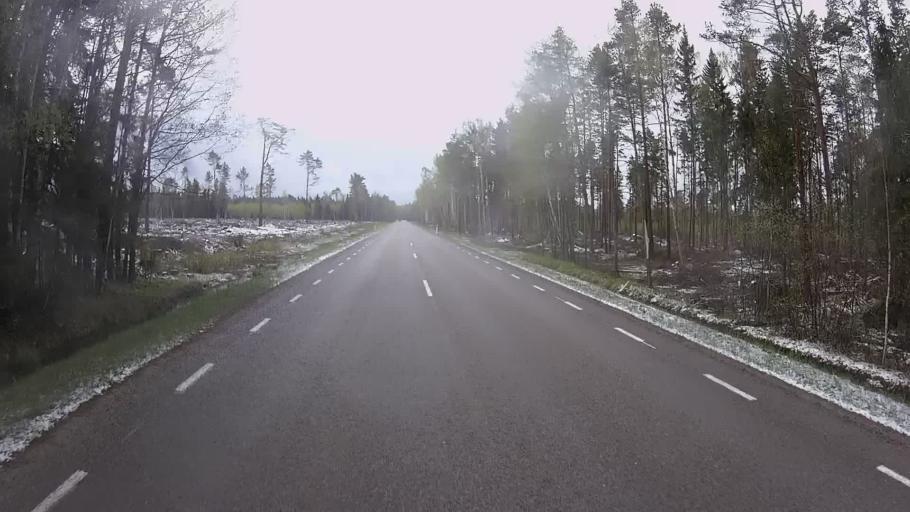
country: EE
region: Hiiumaa
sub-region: Kaerdla linn
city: Kardla
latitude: 58.8302
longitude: 22.4694
